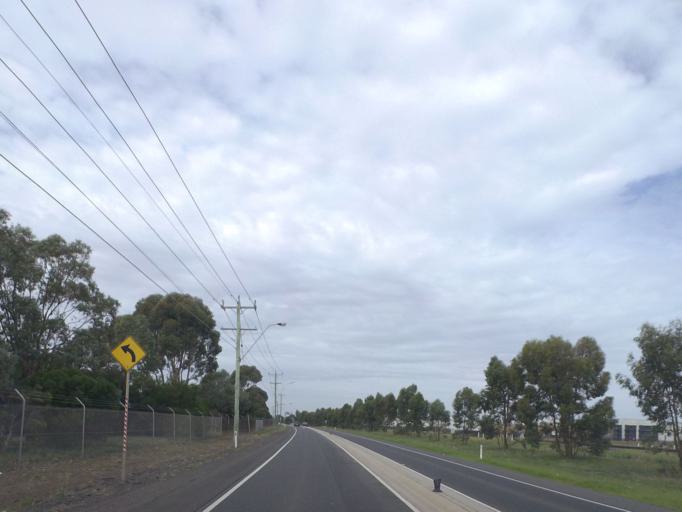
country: AU
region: Victoria
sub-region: Brimbank
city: Deer Park
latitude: -37.7804
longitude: 144.7826
